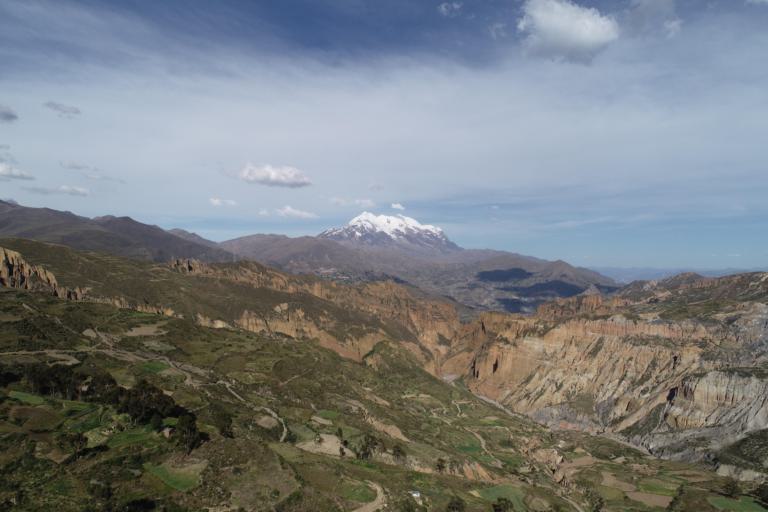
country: BO
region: La Paz
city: La Paz
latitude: -16.5510
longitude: -67.9897
